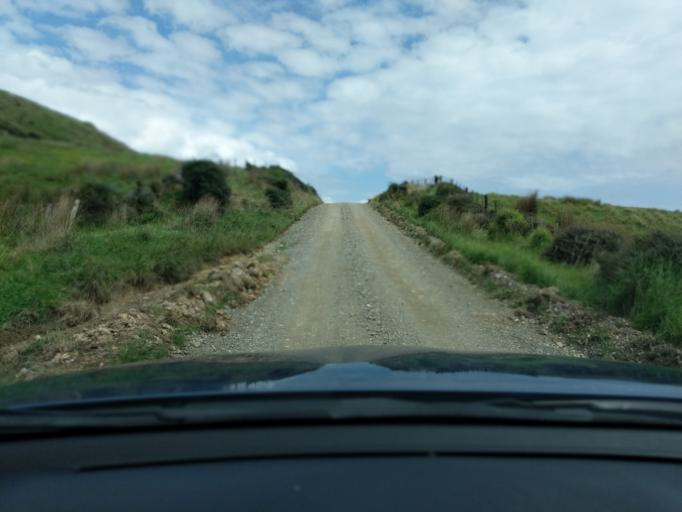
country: NZ
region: Tasman
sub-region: Tasman District
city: Takaka
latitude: -40.6625
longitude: 172.4111
